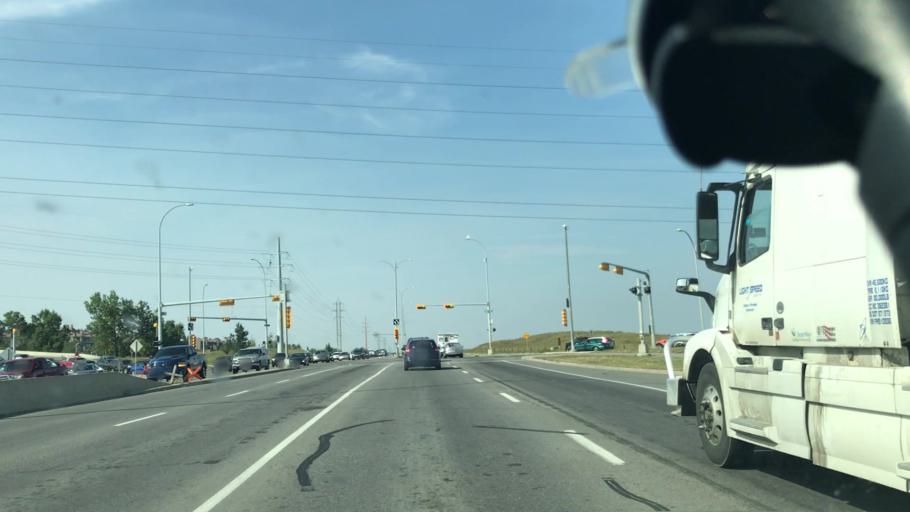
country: CA
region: Alberta
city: Calgary
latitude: 51.0517
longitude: -114.1642
